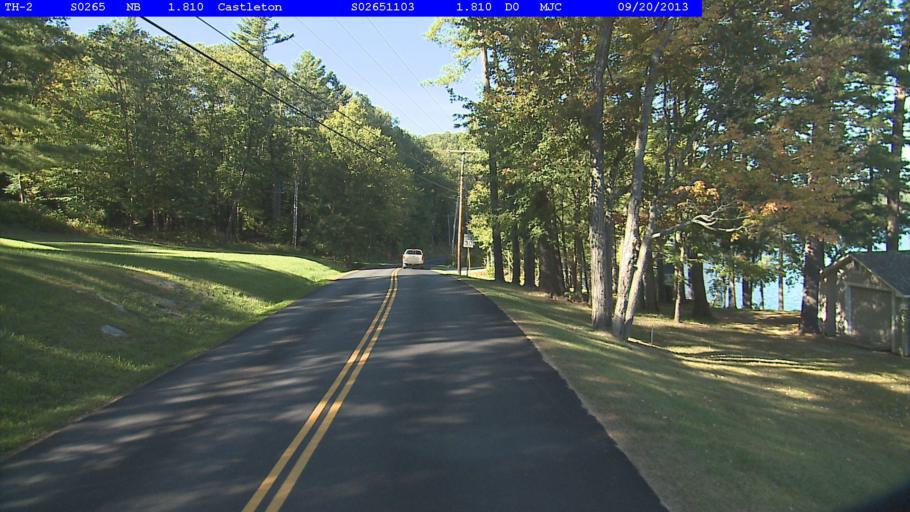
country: US
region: Vermont
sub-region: Rutland County
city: Fair Haven
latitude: 43.6287
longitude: -73.2333
